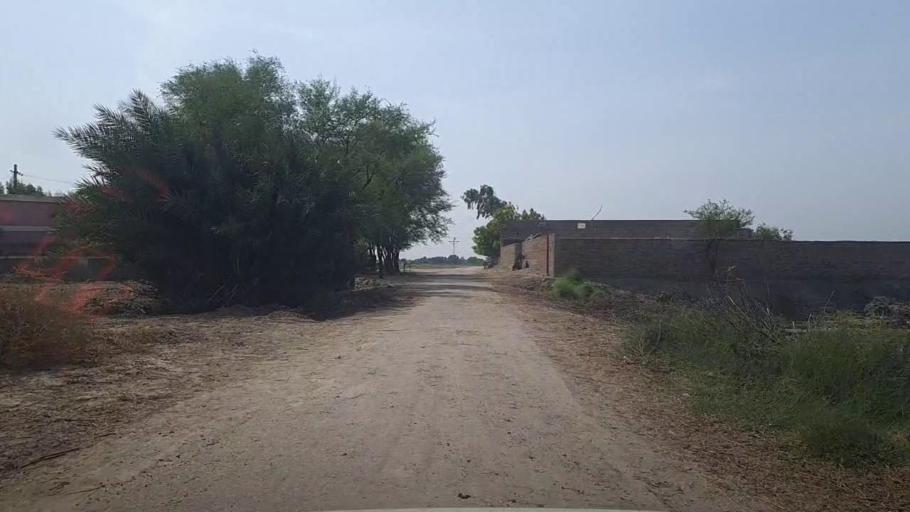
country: PK
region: Sindh
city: Ubauro
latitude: 28.1369
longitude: 69.8249
